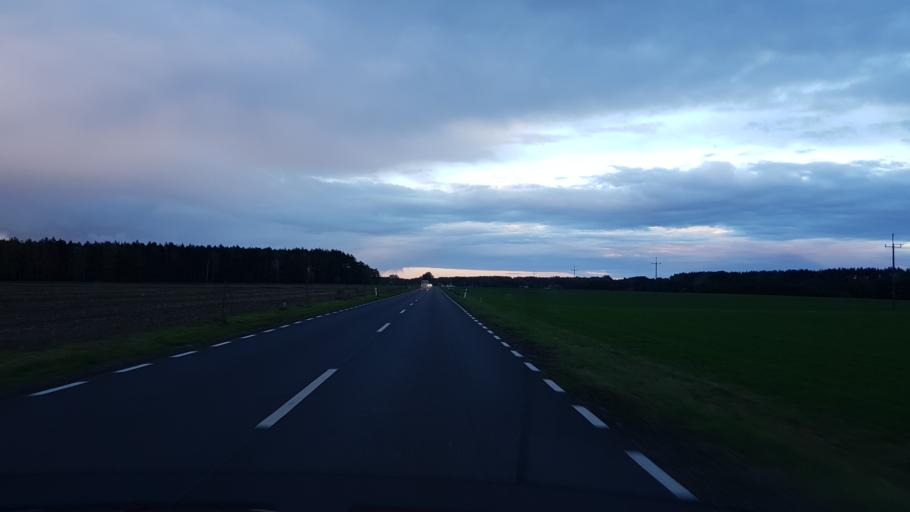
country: PL
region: Greater Poland Voivodeship
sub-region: Powiat zlotowski
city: Krajenka
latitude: 53.2698
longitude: 16.9339
